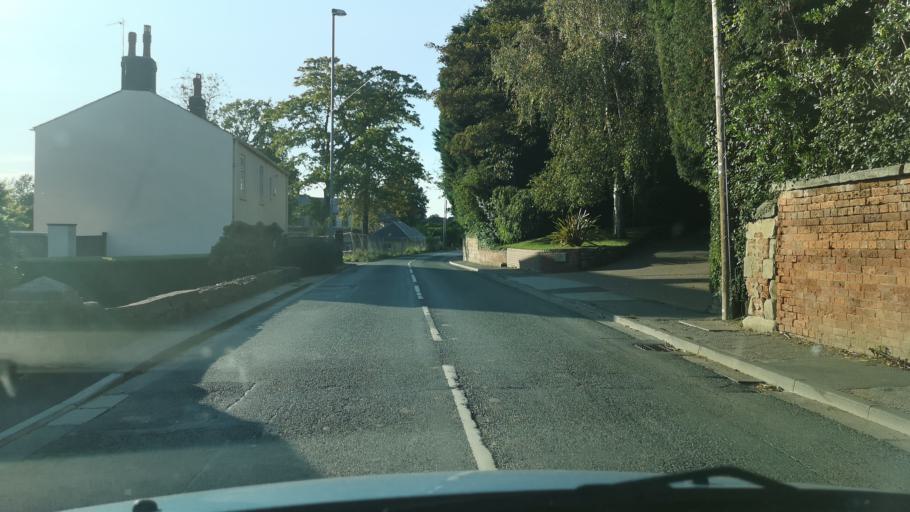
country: GB
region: England
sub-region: City and Borough of Wakefield
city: Darrington
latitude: 53.6746
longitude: -1.2900
